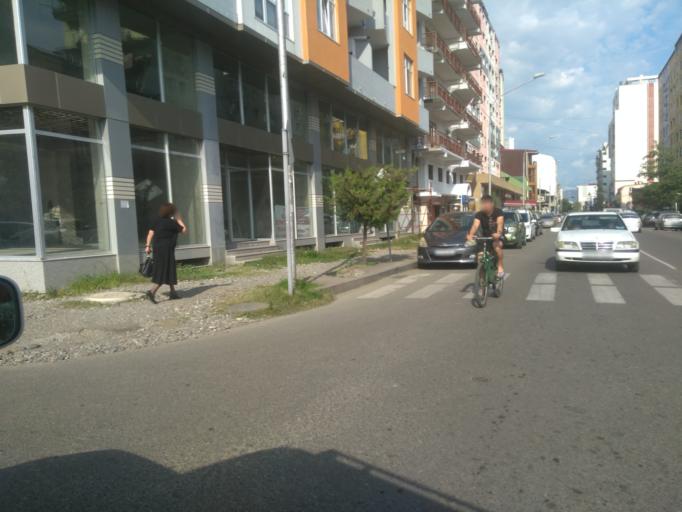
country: GE
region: Ajaria
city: Batumi
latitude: 41.6393
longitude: 41.6259
